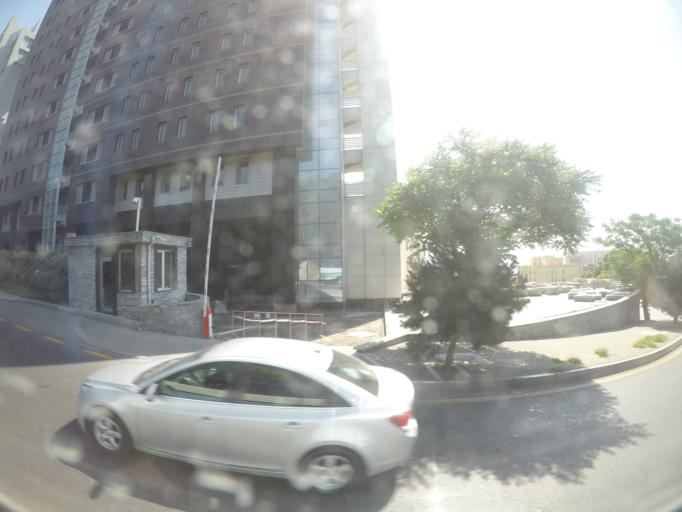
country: AZ
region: Baki
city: Badamdar
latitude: 40.3657
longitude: 49.8255
